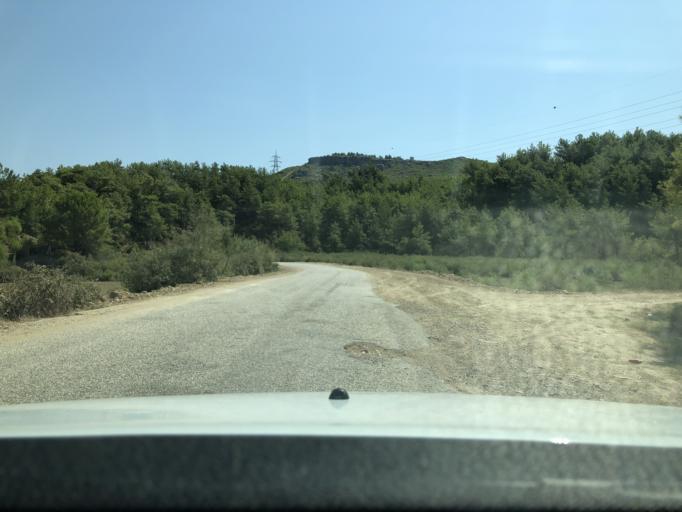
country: TR
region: Antalya
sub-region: Manavgat
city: Manavgat
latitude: 36.8260
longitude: 31.5140
